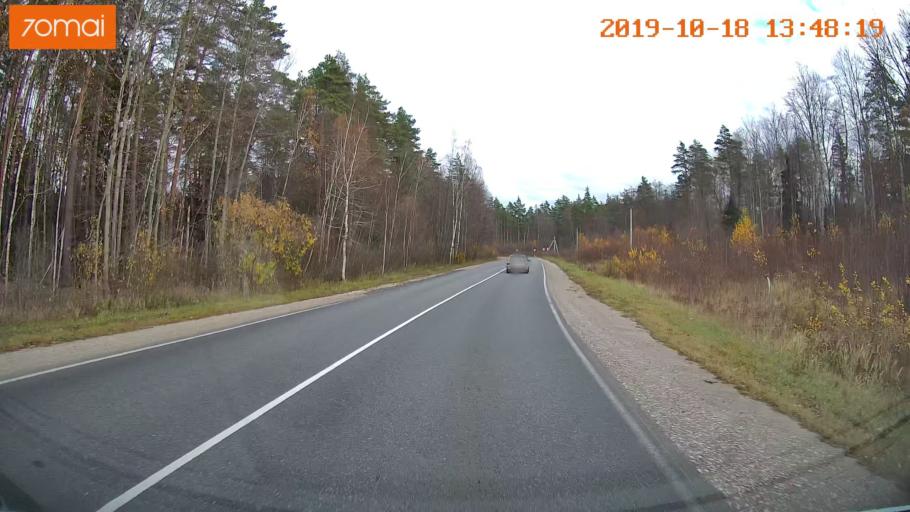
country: RU
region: Moskovskaya
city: Radovitskiy
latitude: 54.9872
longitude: 39.9541
